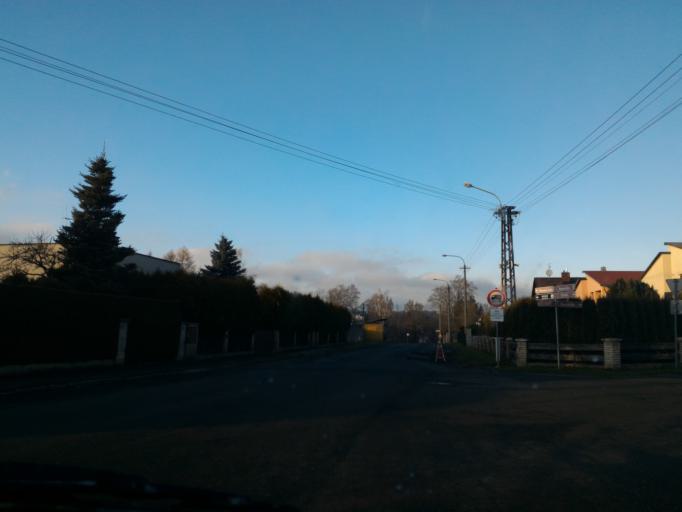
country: CZ
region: Ustecky
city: Varnsdorf
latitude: 50.9149
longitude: 14.6268
